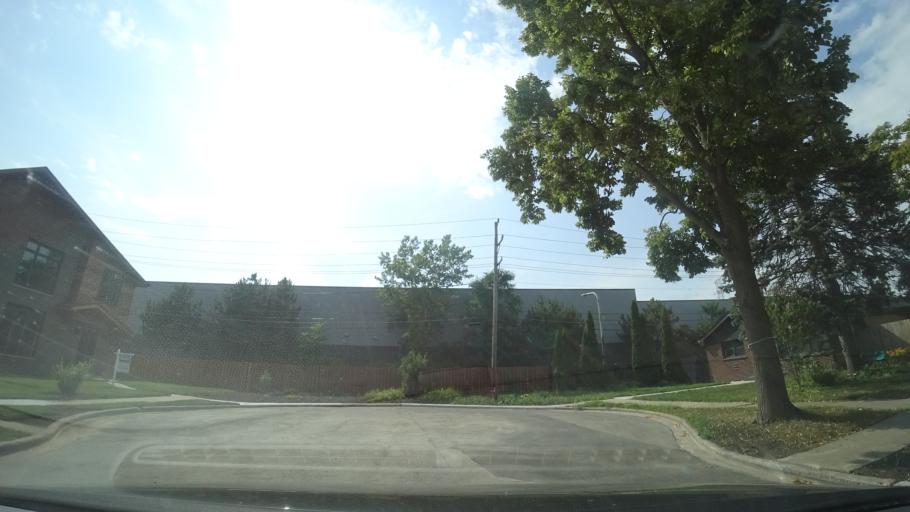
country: US
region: Illinois
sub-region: Cook County
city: Evanston
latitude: 42.0311
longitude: -87.7050
